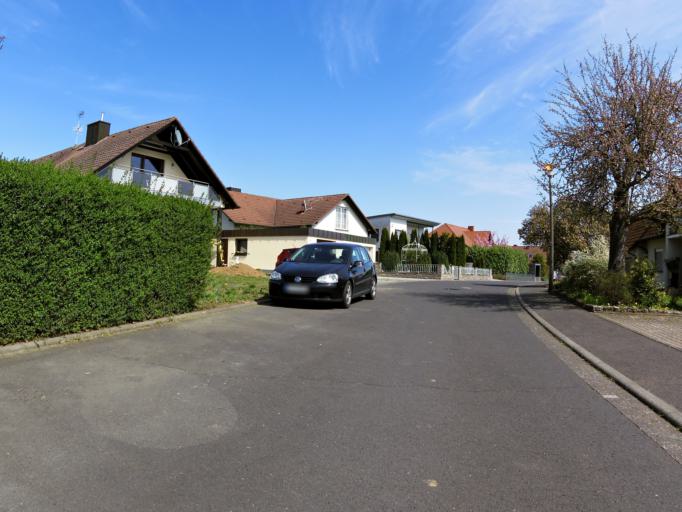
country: DE
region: Bavaria
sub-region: Regierungsbezirk Unterfranken
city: Unterpleichfeld
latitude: 49.8709
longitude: 10.0445
